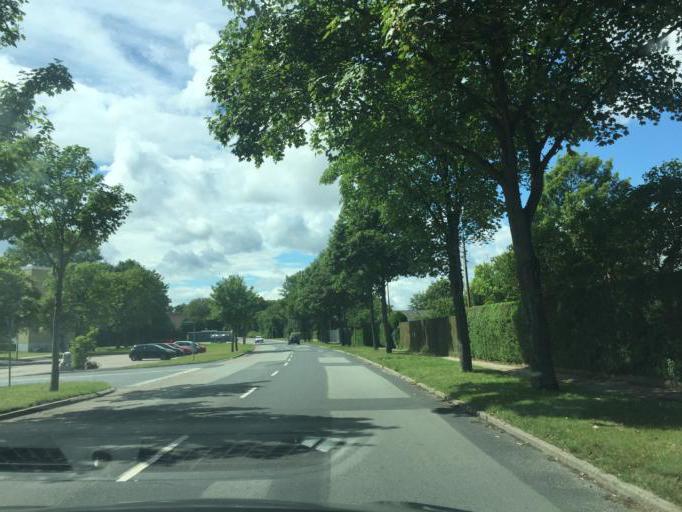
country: DK
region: South Denmark
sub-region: Odense Kommune
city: Odense
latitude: 55.4281
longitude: 10.3701
